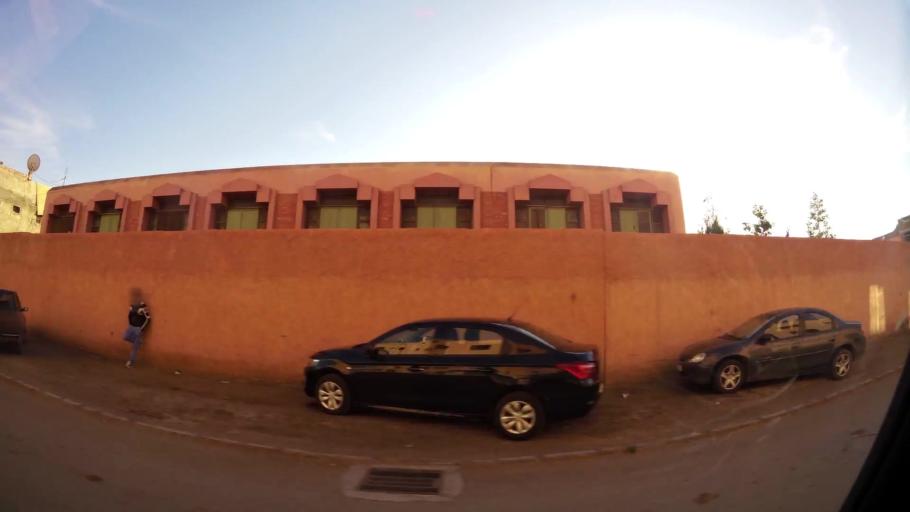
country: MA
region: Marrakech-Tensift-Al Haouz
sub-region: Marrakech
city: Marrakesh
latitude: 31.6186
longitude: -8.0676
